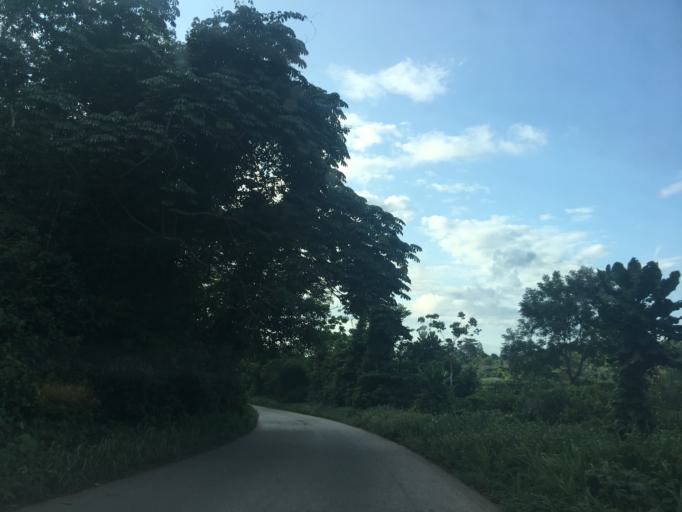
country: GH
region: Western
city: Bibiani
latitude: 6.2795
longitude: -2.2252
